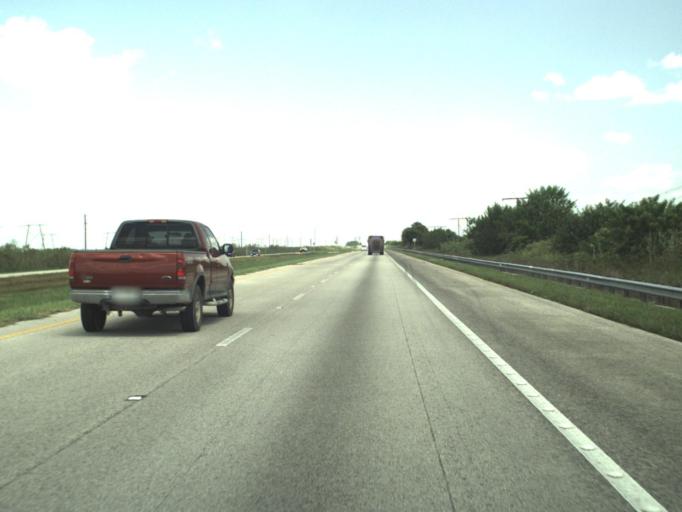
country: US
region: Florida
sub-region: Broward County
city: Weston
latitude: 26.3125
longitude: -80.5203
